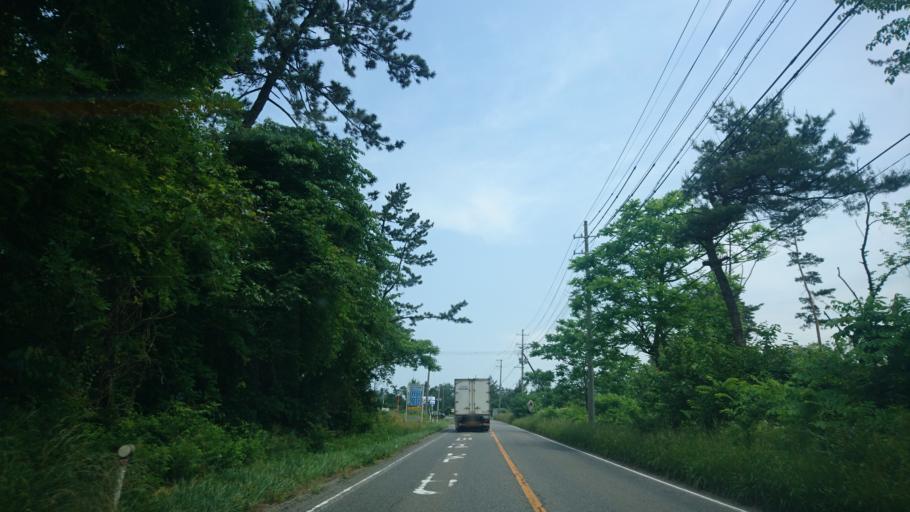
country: JP
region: Niigata
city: Shibata
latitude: 38.0191
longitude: 139.2848
